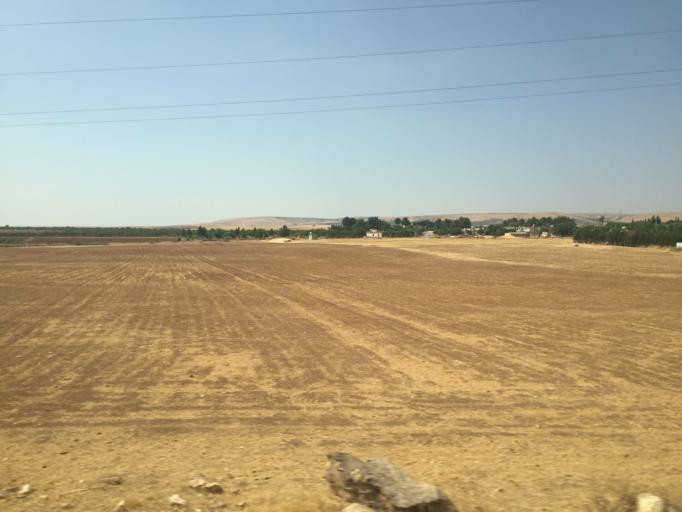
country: TR
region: Sanliurfa
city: Akziyaret
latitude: 37.3836
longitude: 38.8524
